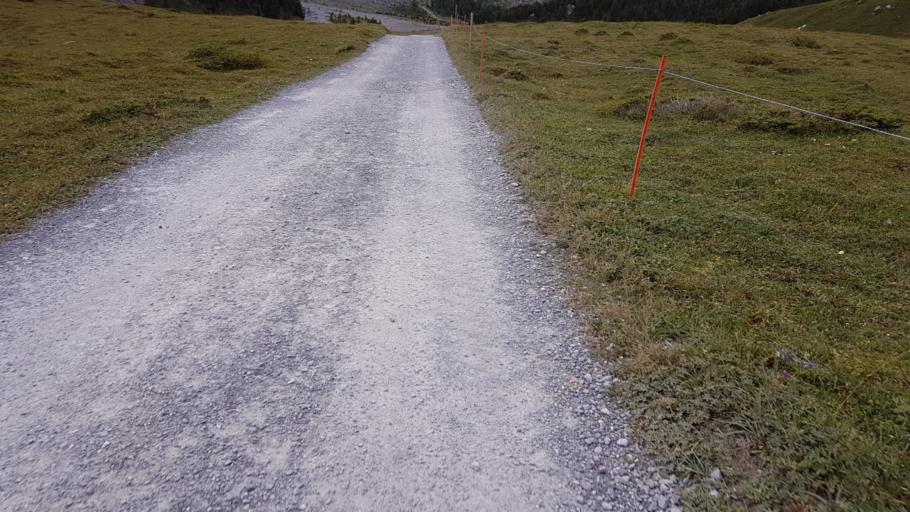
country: CH
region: Bern
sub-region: Frutigen-Niedersimmental District
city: Kandersteg
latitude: 46.4503
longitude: 7.6437
